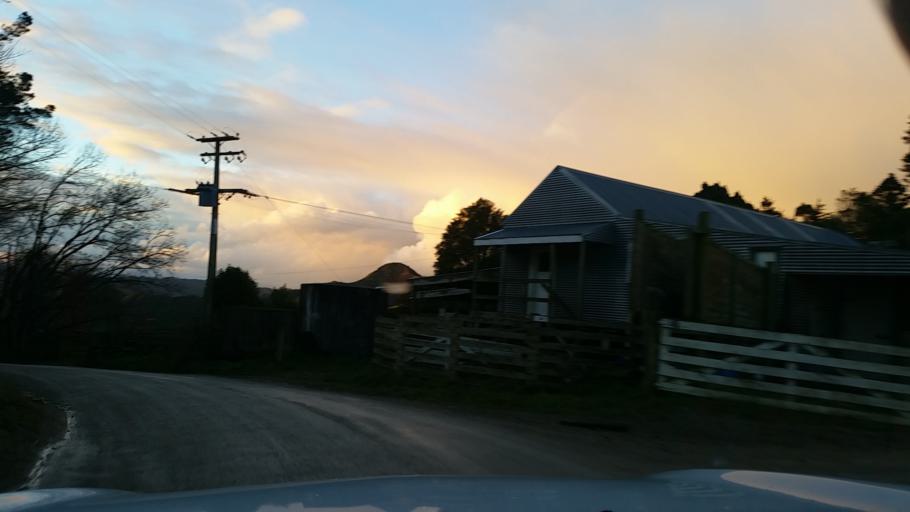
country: NZ
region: Manawatu-Wanganui
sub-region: Wanganui District
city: Wanganui
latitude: -39.7707
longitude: 174.8721
